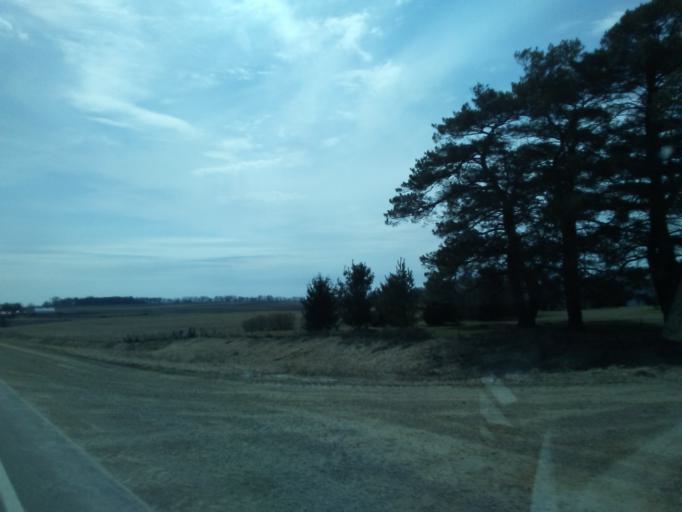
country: US
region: Iowa
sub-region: Winneshiek County
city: Decorah
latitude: 43.4205
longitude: -91.8592
